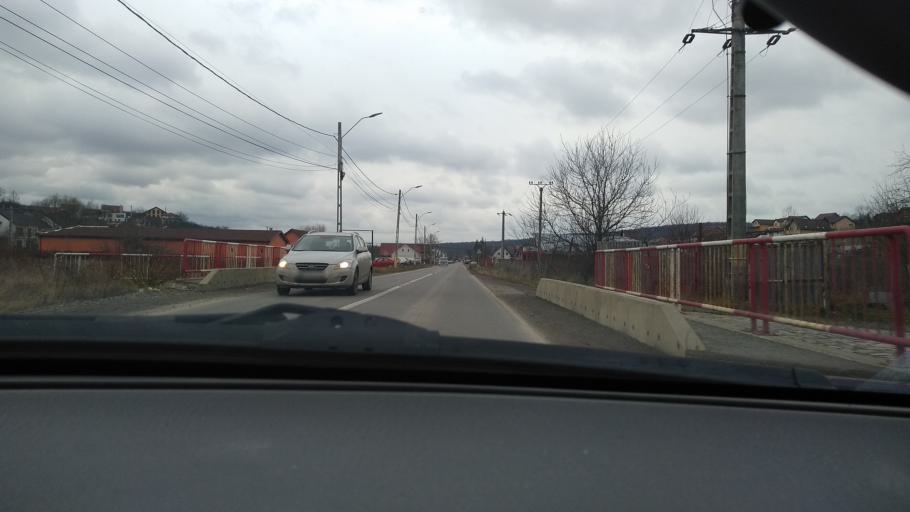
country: RO
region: Mures
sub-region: Comuna Livezeni
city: Livezeni
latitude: 46.5470
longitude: 24.6322
